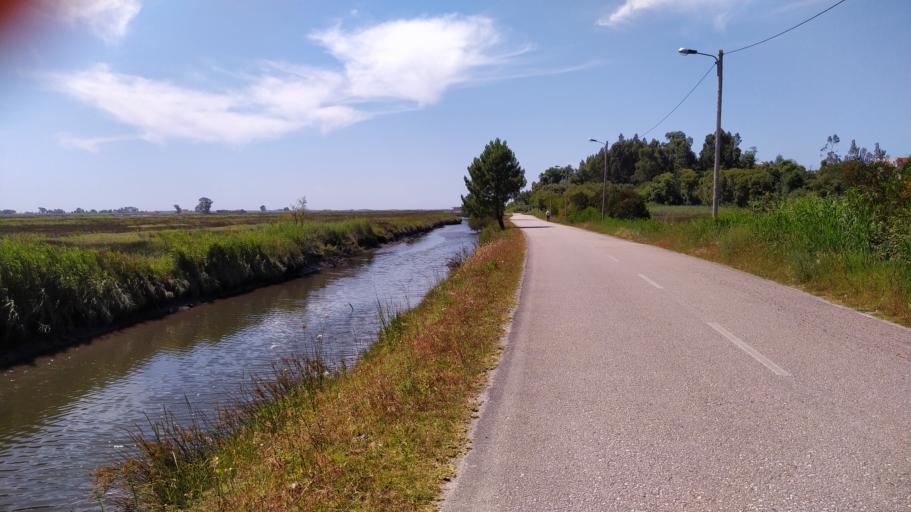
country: PT
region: Aveiro
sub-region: Aveiro
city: Aveiro
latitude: 40.6550
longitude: -8.6324
